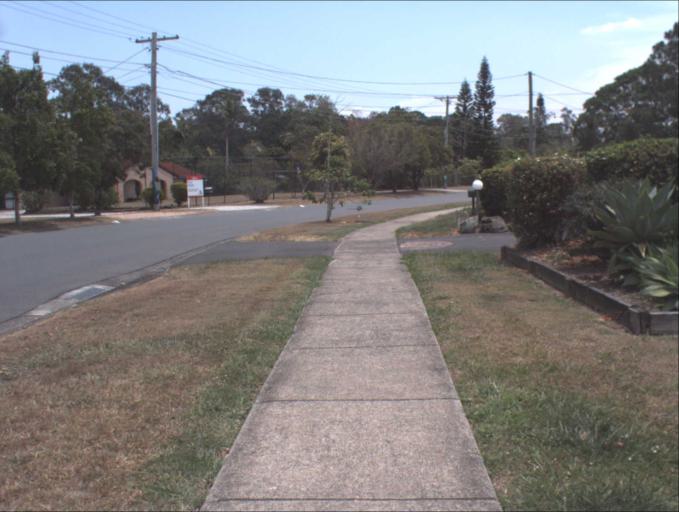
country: AU
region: Queensland
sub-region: Logan
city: Slacks Creek
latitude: -27.6709
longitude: 153.1842
